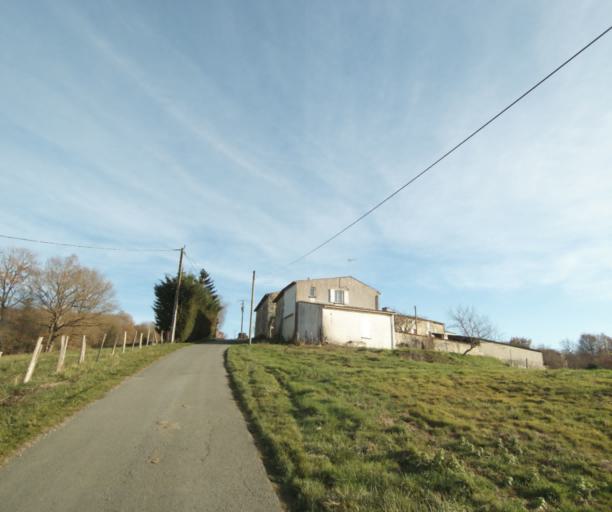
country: FR
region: Poitou-Charentes
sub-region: Departement de la Charente-Maritime
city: Chaniers
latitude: 45.7260
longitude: -0.5324
